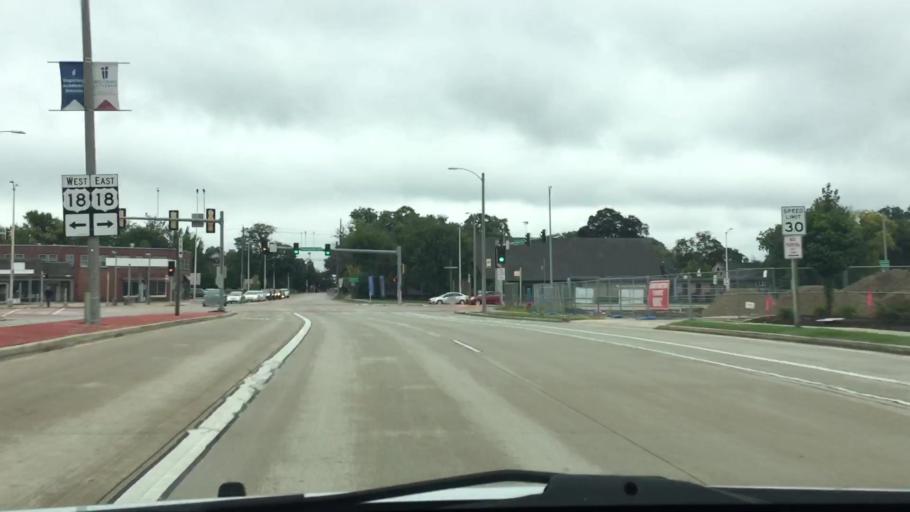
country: US
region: Wisconsin
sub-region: Milwaukee County
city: Wauwatosa
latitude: 43.0352
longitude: -88.0162
